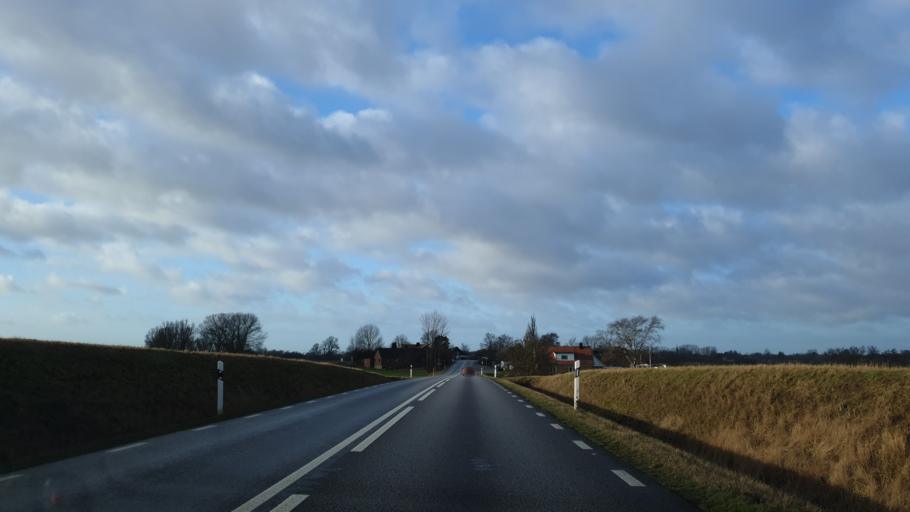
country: SE
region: Skane
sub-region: Trelleborgs Kommun
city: Trelleborg
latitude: 55.4599
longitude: 13.1574
